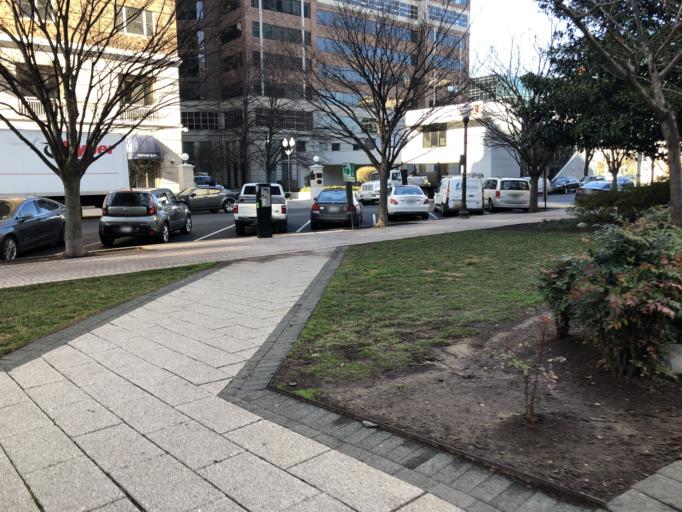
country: US
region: Virginia
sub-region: Arlington County
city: Arlington
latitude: 38.8812
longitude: -77.1125
